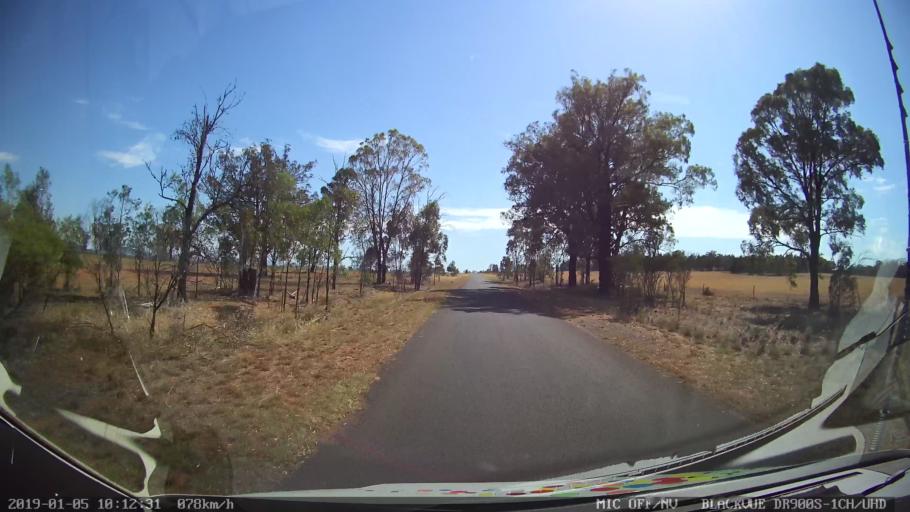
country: AU
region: New South Wales
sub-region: Gilgandra
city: Gilgandra
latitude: -31.6073
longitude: 148.9139
